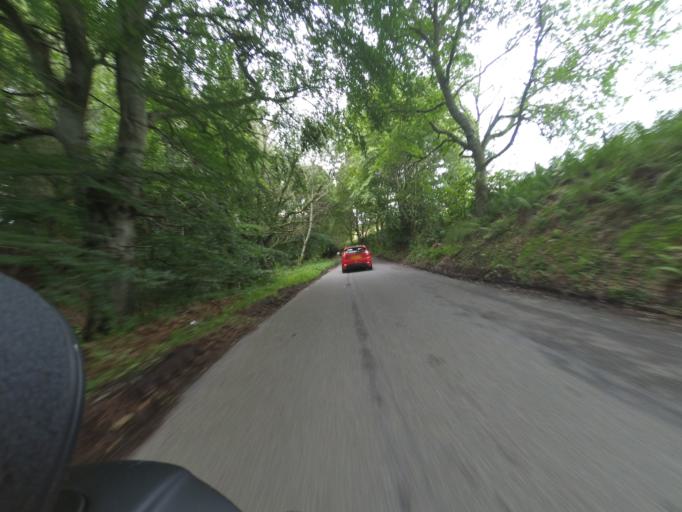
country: GB
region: Scotland
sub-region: Highland
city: Inverness
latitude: 57.5109
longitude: -4.2588
